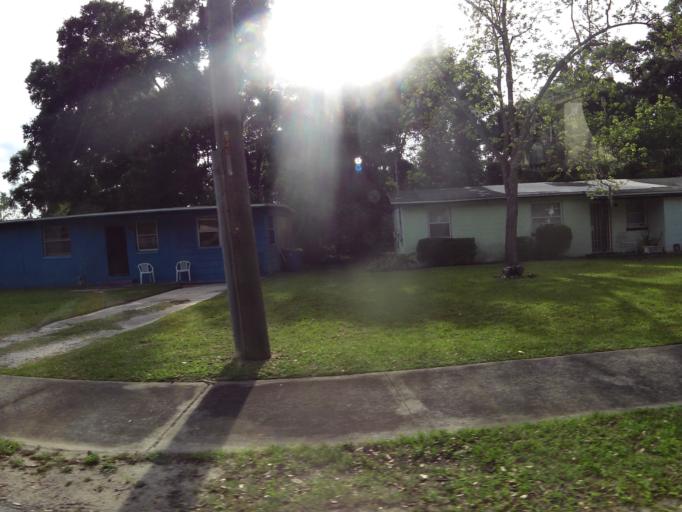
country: US
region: Florida
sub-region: Duval County
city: Jacksonville
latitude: 30.3297
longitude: -81.5945
